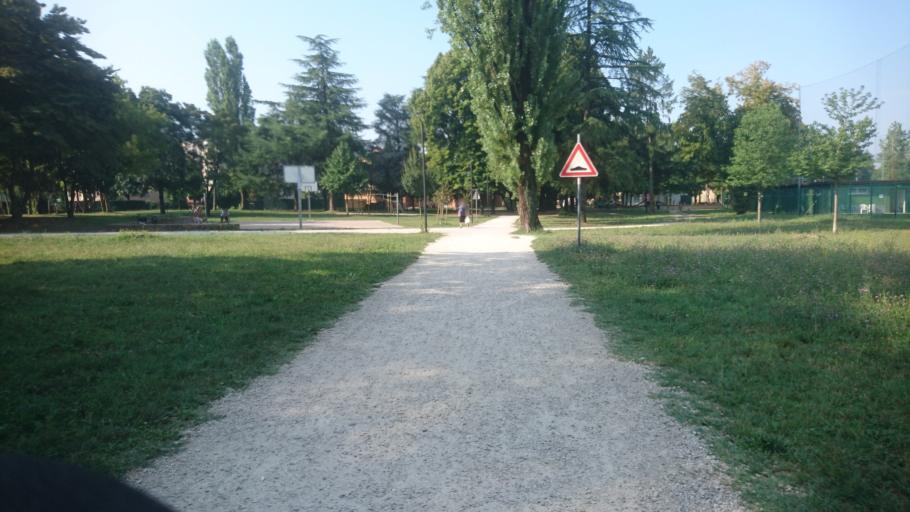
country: IT
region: Veneto
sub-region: Provincia di Padova
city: Padova
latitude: 45.4199
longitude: 11.8895
